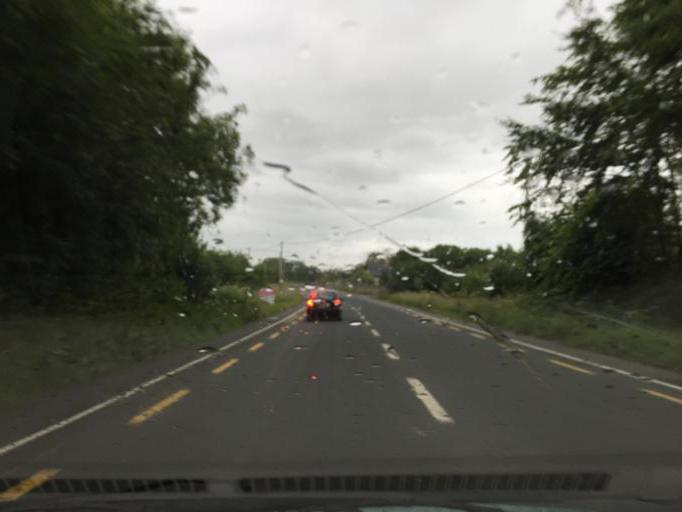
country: IE
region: Connaught
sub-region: Sligo
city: Strandhill
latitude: 54.2727
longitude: -8.5495
